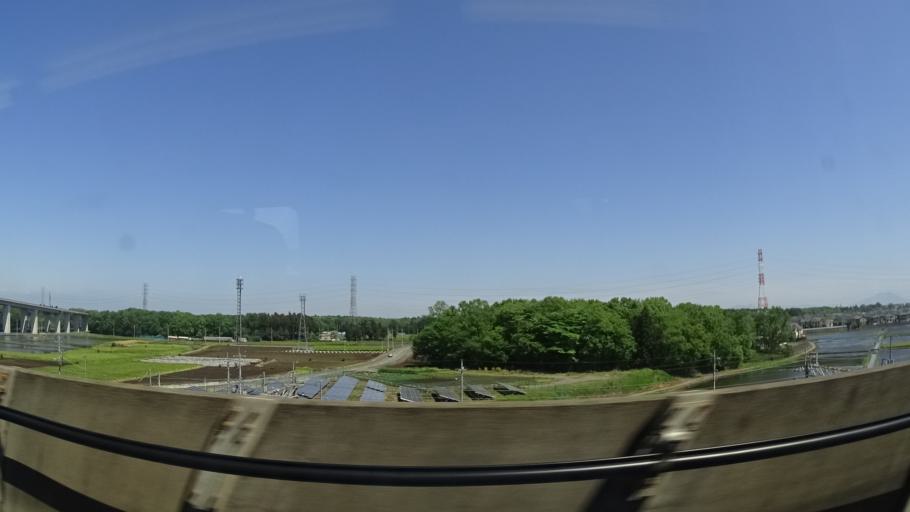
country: JP
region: Tochigi
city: Kaminokawa
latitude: 36.4621
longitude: 139.8715
